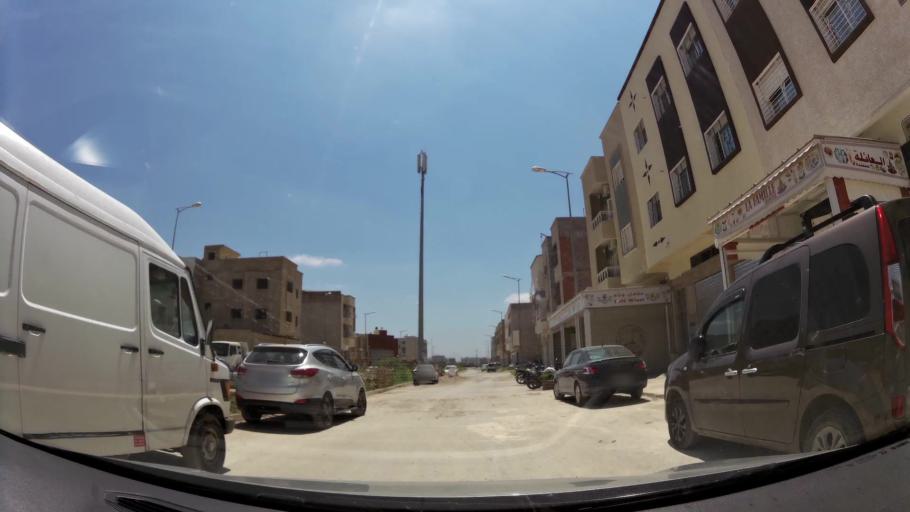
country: MA
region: Fes-Boulemane
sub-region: Fes
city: Fes
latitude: 34.0308
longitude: -5.0506
